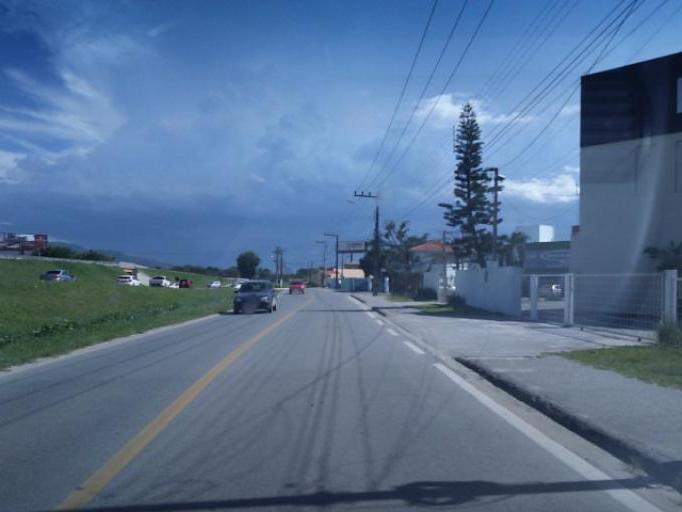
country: BR
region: Santa Catarina
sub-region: Itapema
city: Itapema
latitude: -27.1314
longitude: -48.6103
